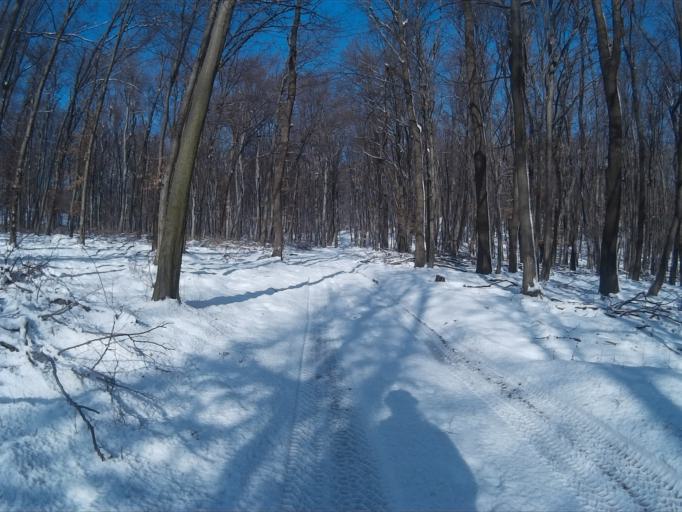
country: HU
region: Komarom-Esztergom
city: Labatlan
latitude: 47.7041
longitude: 18.5120
